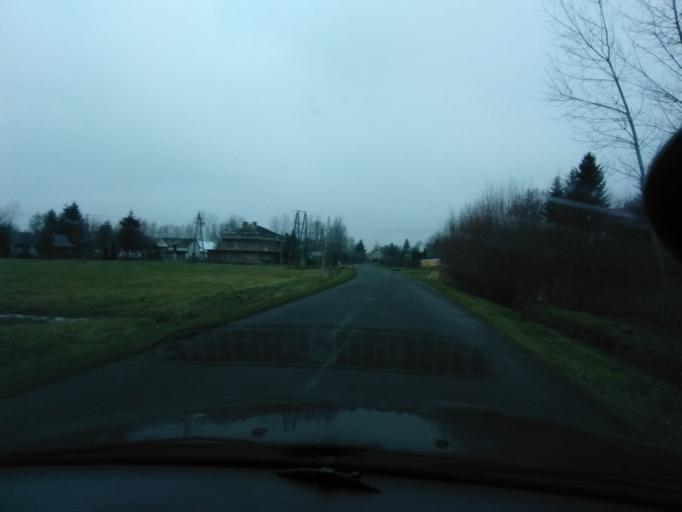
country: PL
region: Subcarpathian Voivodeship
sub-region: Powiat przeworski
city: Zarzecze
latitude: 49.9550
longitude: 22.5668
